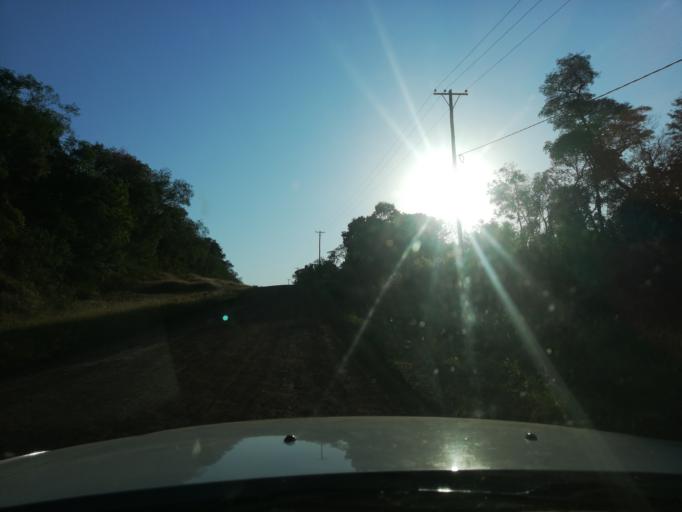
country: AR
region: Misiones
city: Cerro Cora
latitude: -27.6304
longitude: -55.7084
